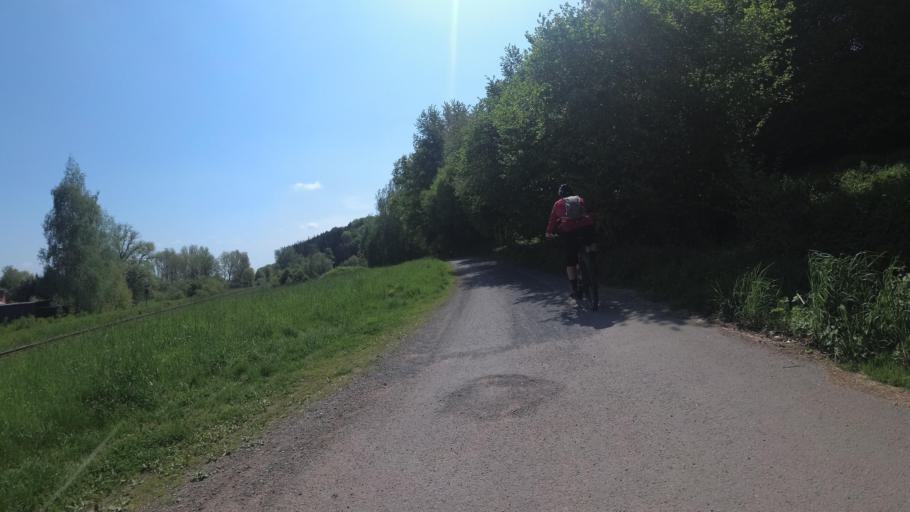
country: DE
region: Rheinland-Pfalz
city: Steinwenden
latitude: 49.4556
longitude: 7.5022
